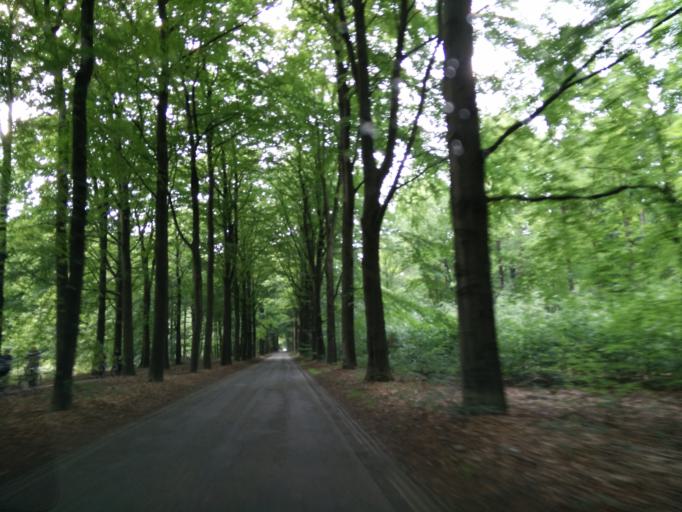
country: NL
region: Drenthe
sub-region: Gemeente Aa en Hunze
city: Anloo
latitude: 52.9812
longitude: 6.7369
